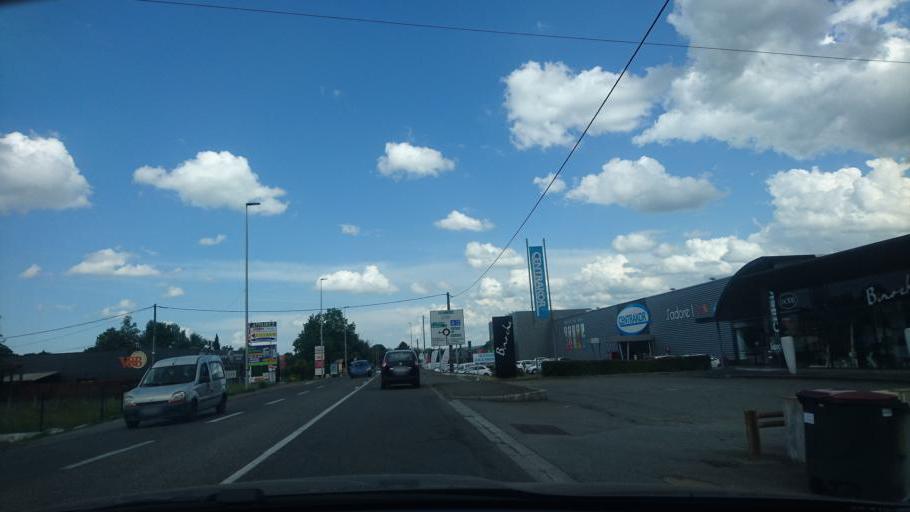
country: FR
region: Midi-Pyrenees
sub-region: Departement des Hautes-Pyrenees
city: Ibos
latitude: 43.2383
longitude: 0.0380
